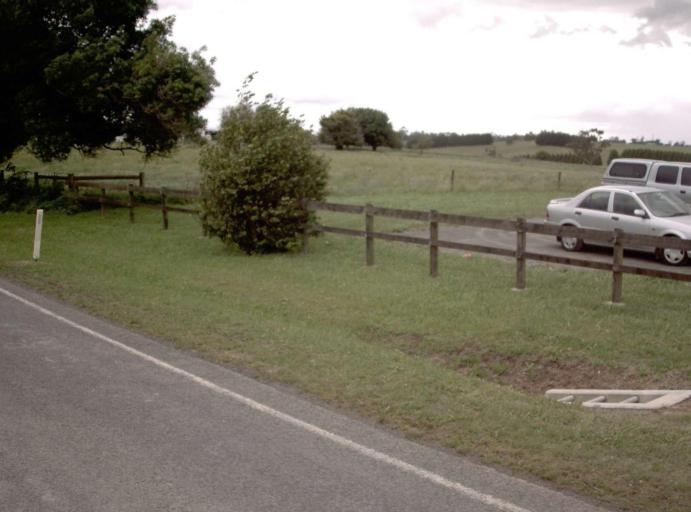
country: AU
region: Victoria
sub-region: Baw Baw
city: Warragul
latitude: -38.1322
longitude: 145.9858
